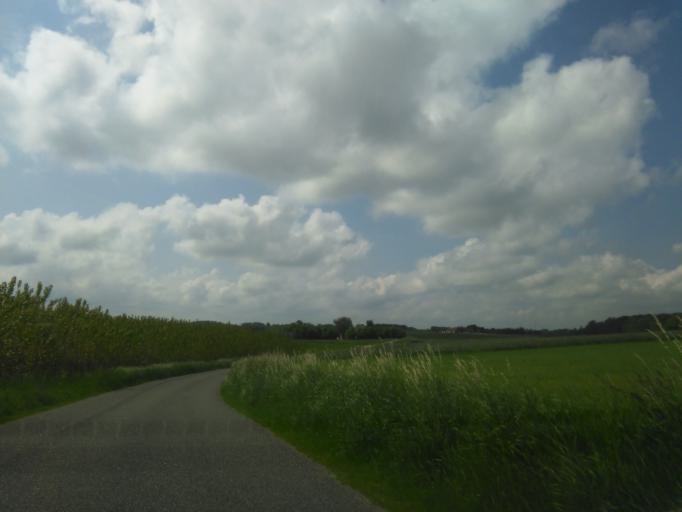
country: DK
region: Central Jutland
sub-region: Skanderborg Kommune
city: Skovby
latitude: 56.2108
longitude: 9.9735
